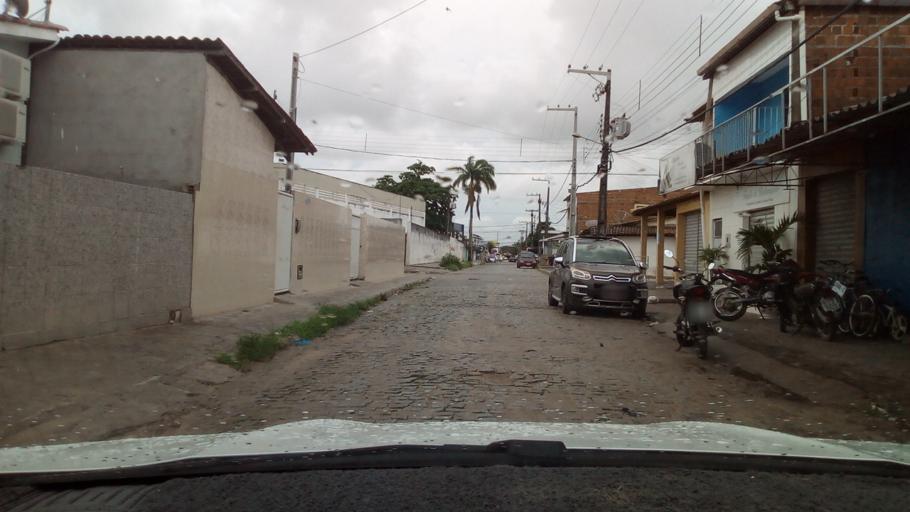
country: BR
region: Paraiba
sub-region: Joao Pessoa
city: Joao Pessoa
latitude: -7.1491
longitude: -34.8720
